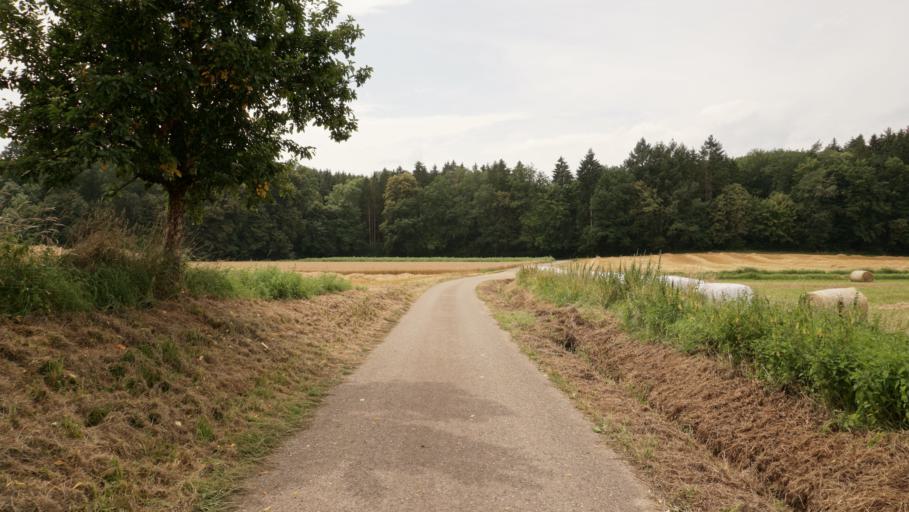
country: DE
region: Baden-Wuerttemberg
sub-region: Karlsruhe Region
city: Billigheim
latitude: 49.3253
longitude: 9.2074
